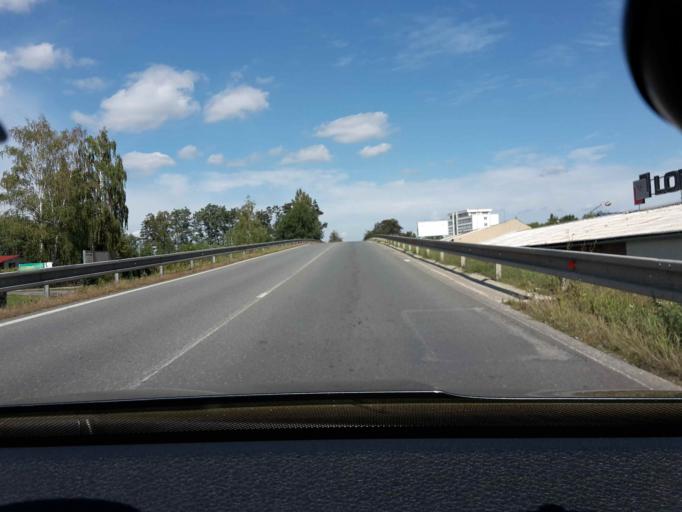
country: CZ
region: Jihocesky
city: Sobeslav
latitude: 49.2650
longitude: 14.7132
